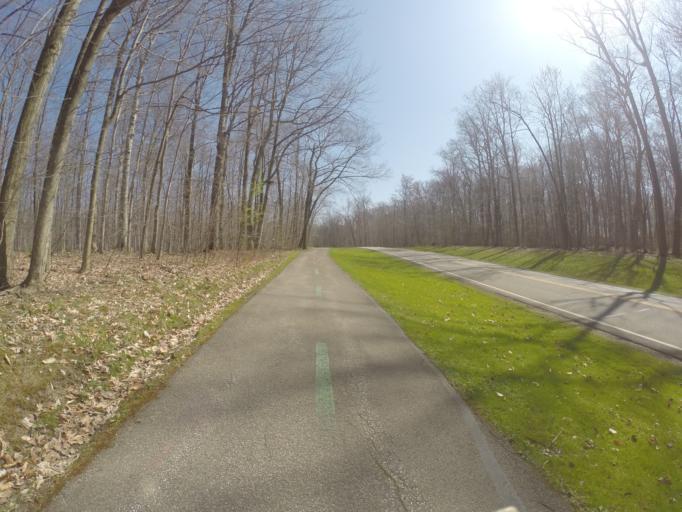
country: US
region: Ohio
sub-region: Lake County
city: Willoughby Hills
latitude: 41.5845
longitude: -81.4288
